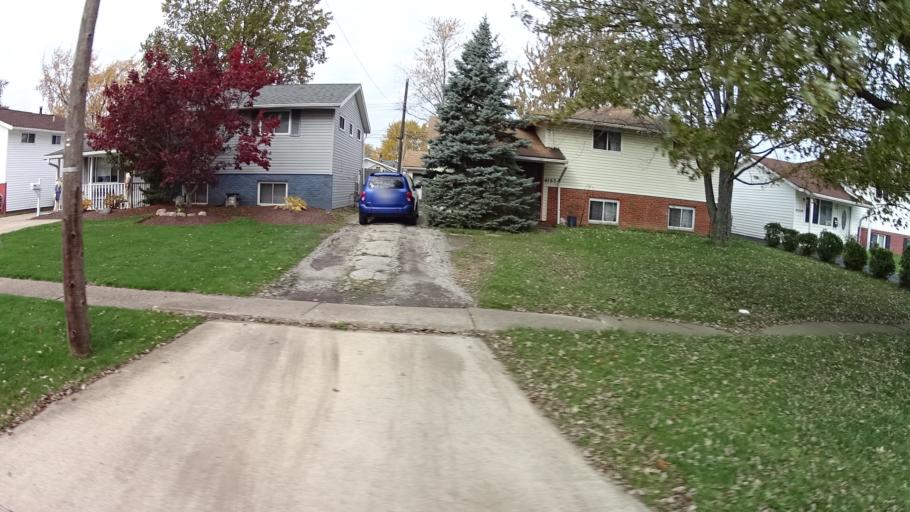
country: US
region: Ohio
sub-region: Lorain County
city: Sheffield Lake
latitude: 41.4794
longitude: -82.1106
